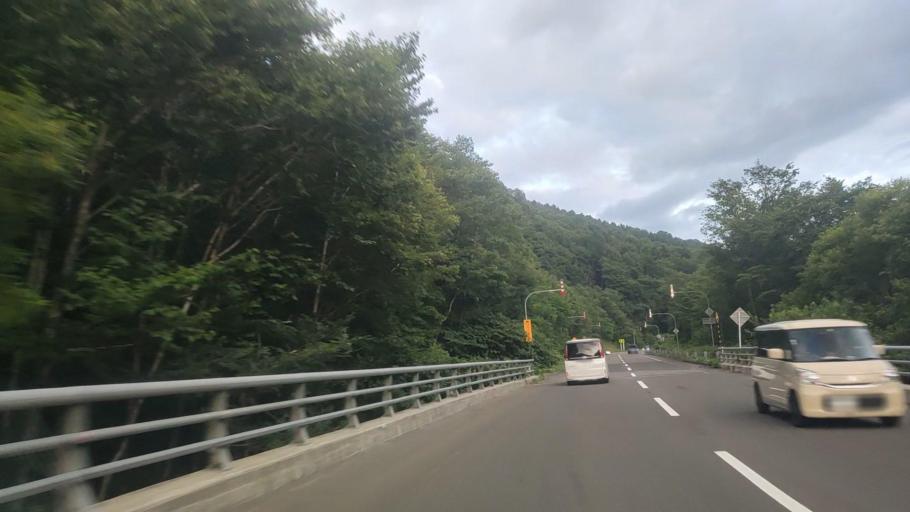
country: JP
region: Hokkaido
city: Shimo-furano
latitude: 43.3619
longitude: 142.2414
